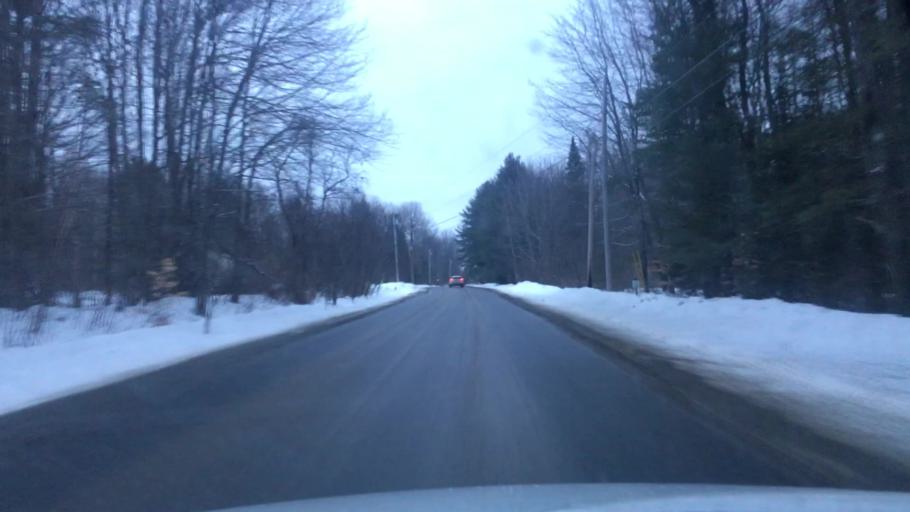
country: US
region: Maine
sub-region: Kennebec County
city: Oakland
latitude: 44.6296
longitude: -69.7319
